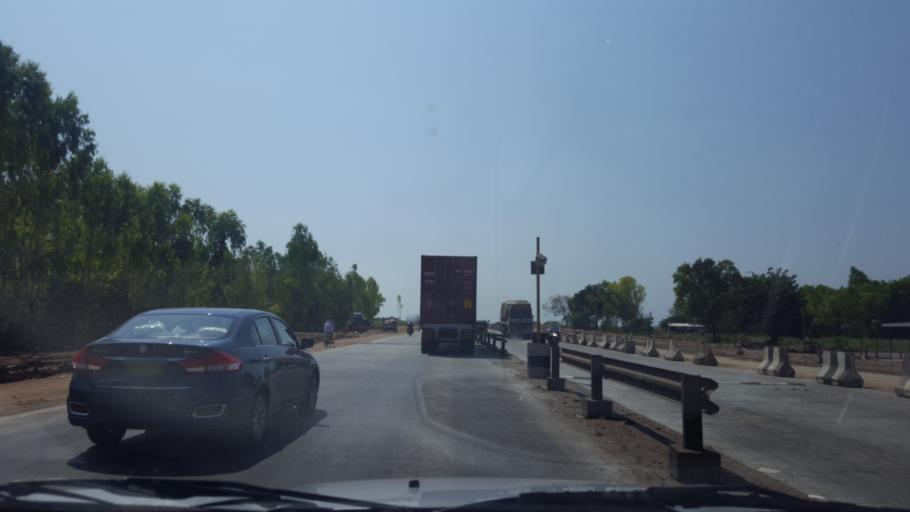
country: IN
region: Andhra Pradesh
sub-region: Prakasam
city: Addanki
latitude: 15.7886
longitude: 80.0378
